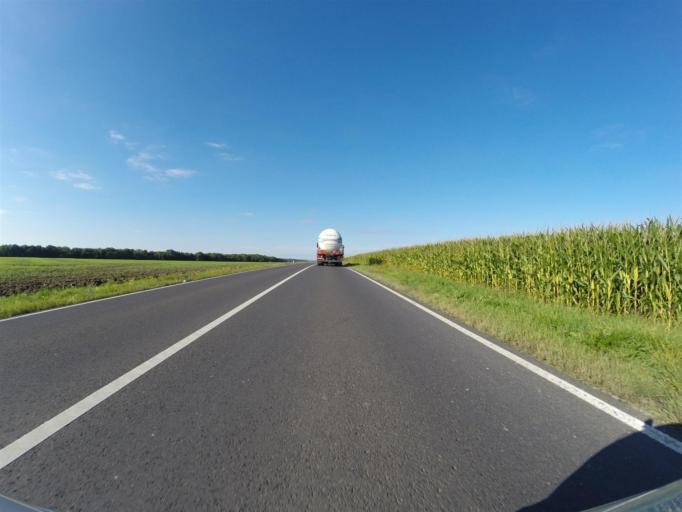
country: DE
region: Thuringia
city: Grossschwabhausen
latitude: 50.9527
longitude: 11.5052
